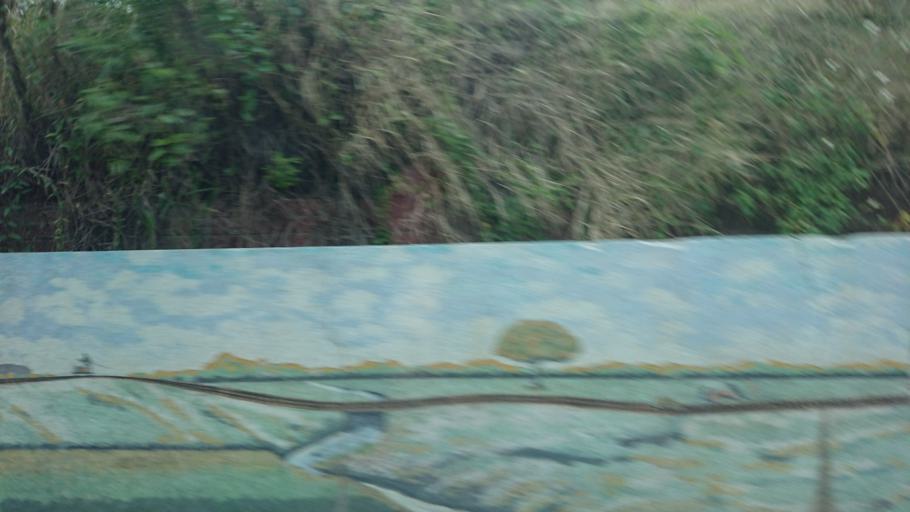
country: TW
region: Taiwan
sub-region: Hsinchu
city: Hsinchu
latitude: 24.8378
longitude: 120.9445
